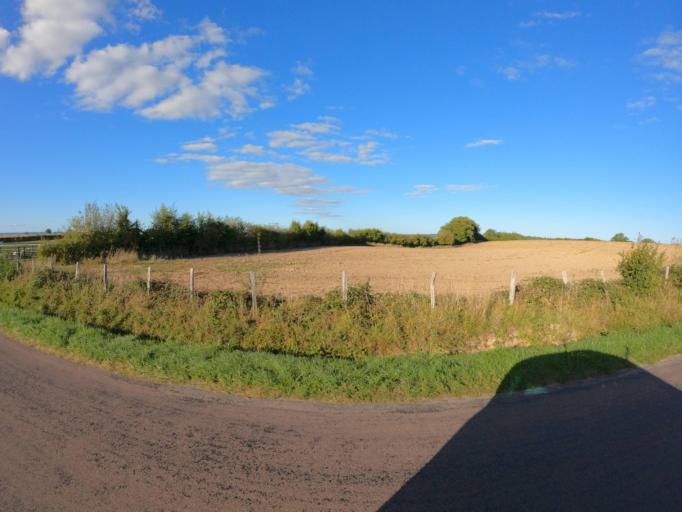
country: FR
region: Bourgogne
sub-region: Departement de Saone-et-Loire
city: Ecuisses
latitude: 46.7451
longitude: 4.5436
